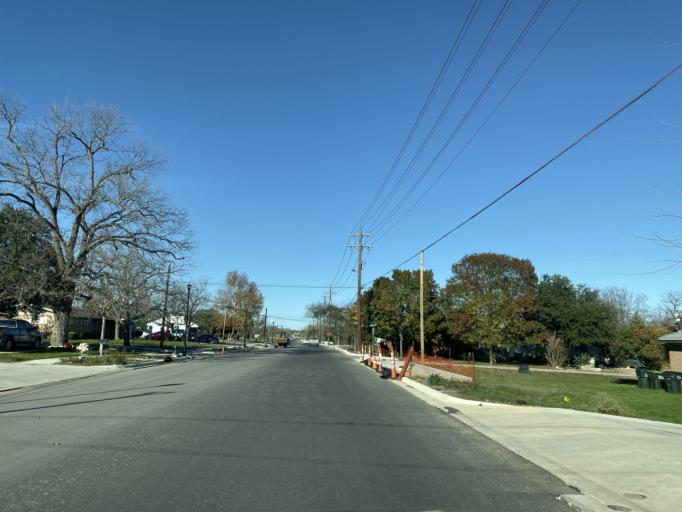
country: US
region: Texas
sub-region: Hays County
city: Kyle
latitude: 29.9919
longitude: -97.8766
